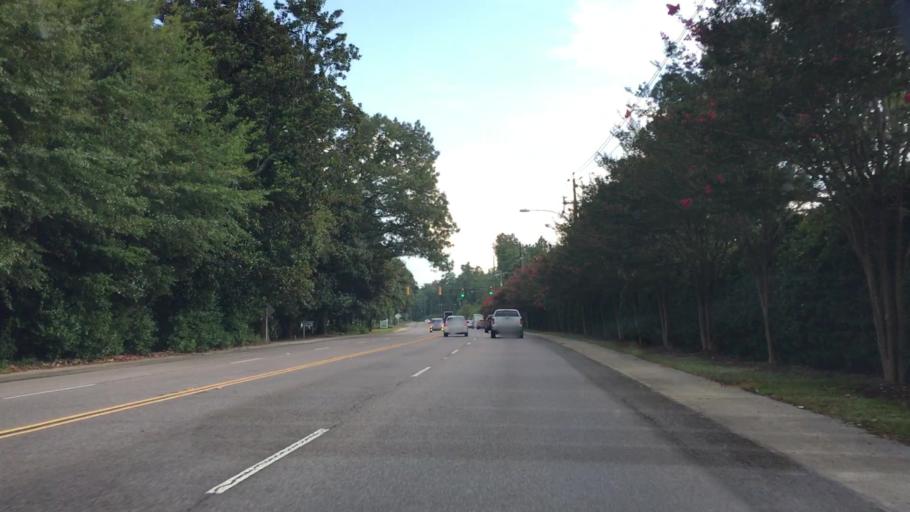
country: US
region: South Carolina
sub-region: Aiken County
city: Aiken
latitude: 33.5400
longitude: -81.7233
